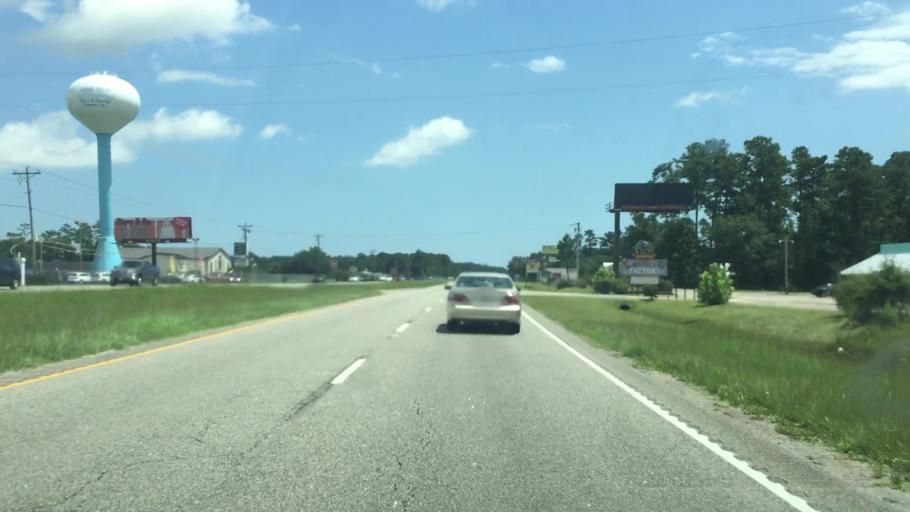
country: US
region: South Carolina
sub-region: Horry County
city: North Myrtle Beach
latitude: 33.9036
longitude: -78.7027
